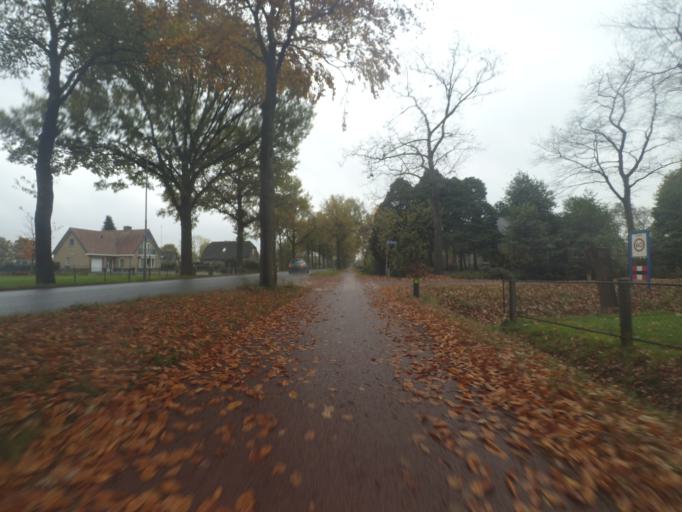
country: NL
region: Gelderland
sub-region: Gemeente Ede
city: Lunteren
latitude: 52.0672
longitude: 5.6359
